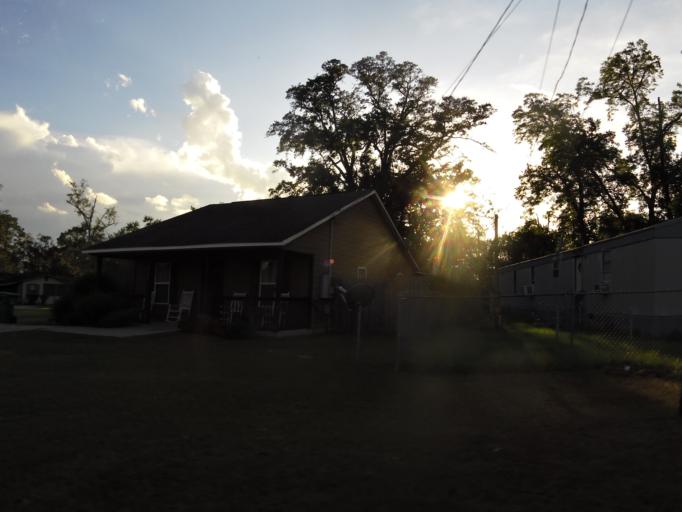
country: US
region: Georgia
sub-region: Lowndes County
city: Valdosta
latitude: 30.8264
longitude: -83.2735
